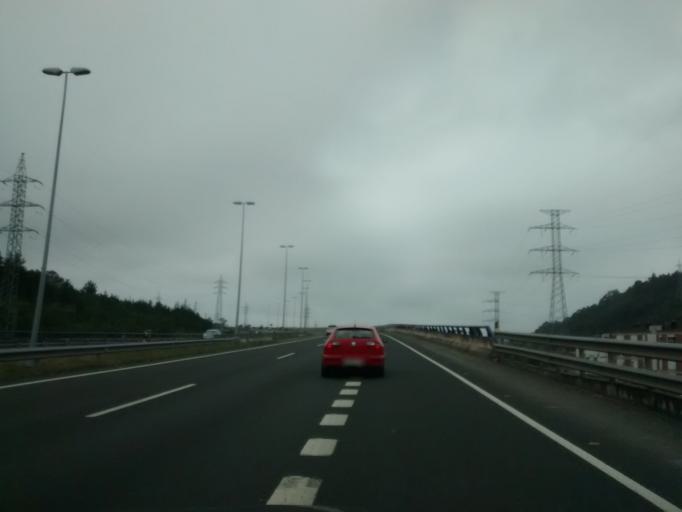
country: ES
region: Cantabria
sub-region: Provincia de Cantabria
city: Torrelavega
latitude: 43.3567
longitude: -4.0693
